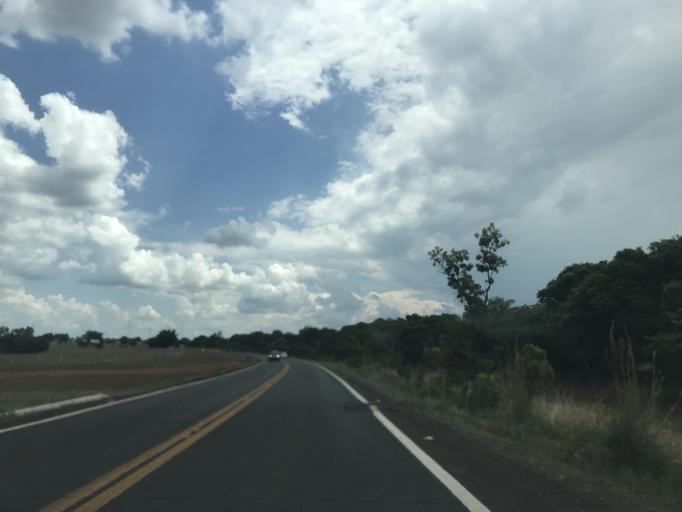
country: BR
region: Goias
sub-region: Caldas Novas
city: Caldas Novas
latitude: -17.6537
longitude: -48.7090
